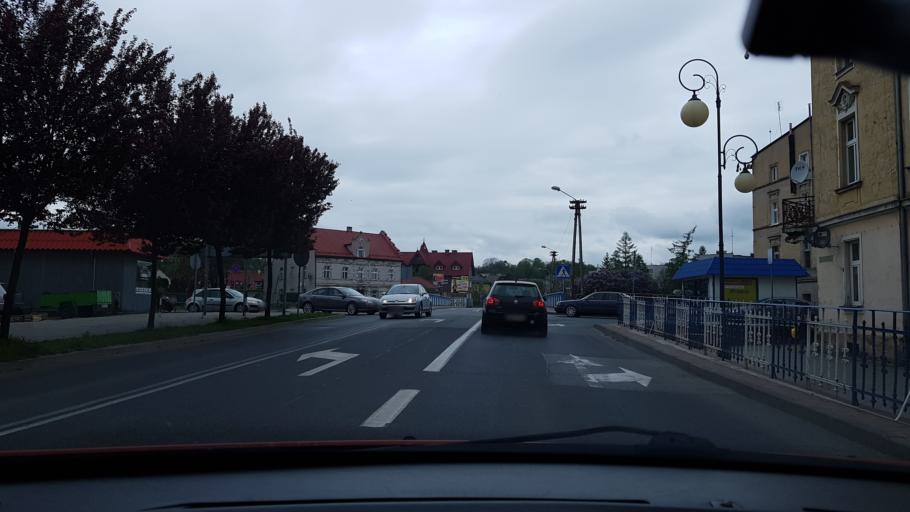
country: PL
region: Opole Voivodeship
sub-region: Powiat nyski
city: Glucholazy
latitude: 50.3160
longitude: 17.3810
